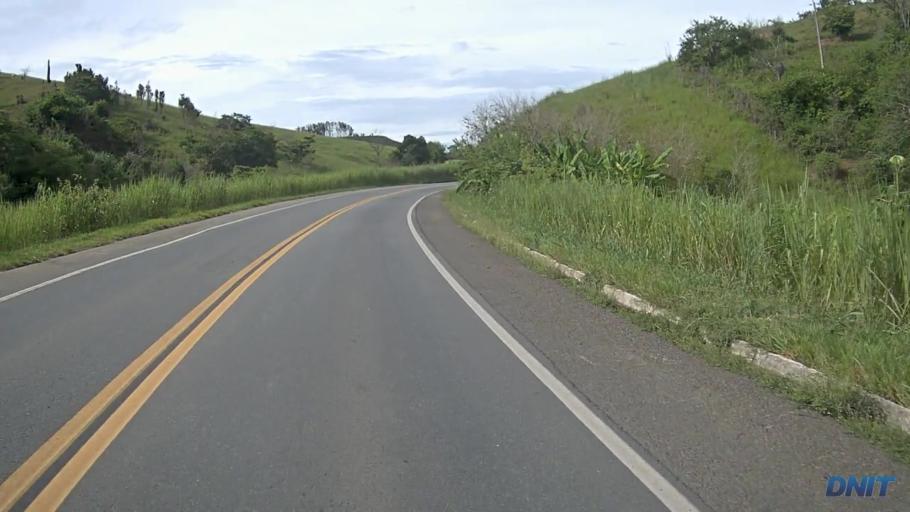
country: BR
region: Minas Gerais
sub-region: Belo Oriente
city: Belo Oriente
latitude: -19.2131
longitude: -42.3065
